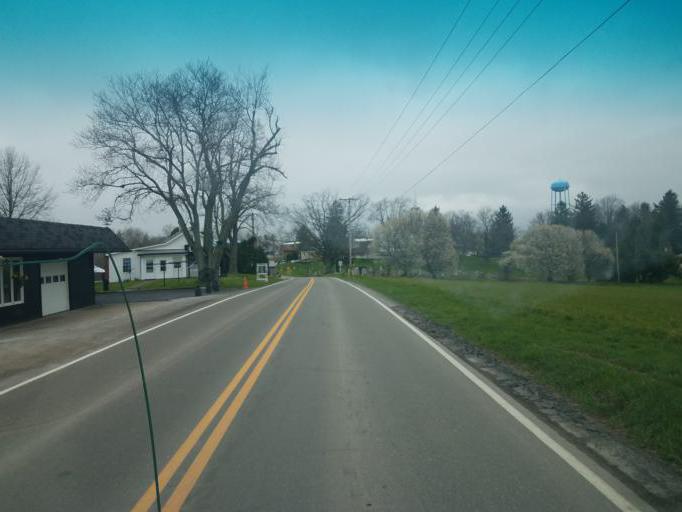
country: US
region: Ohio
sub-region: Stark County
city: Beach City
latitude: 40.6152
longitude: -81.6916
